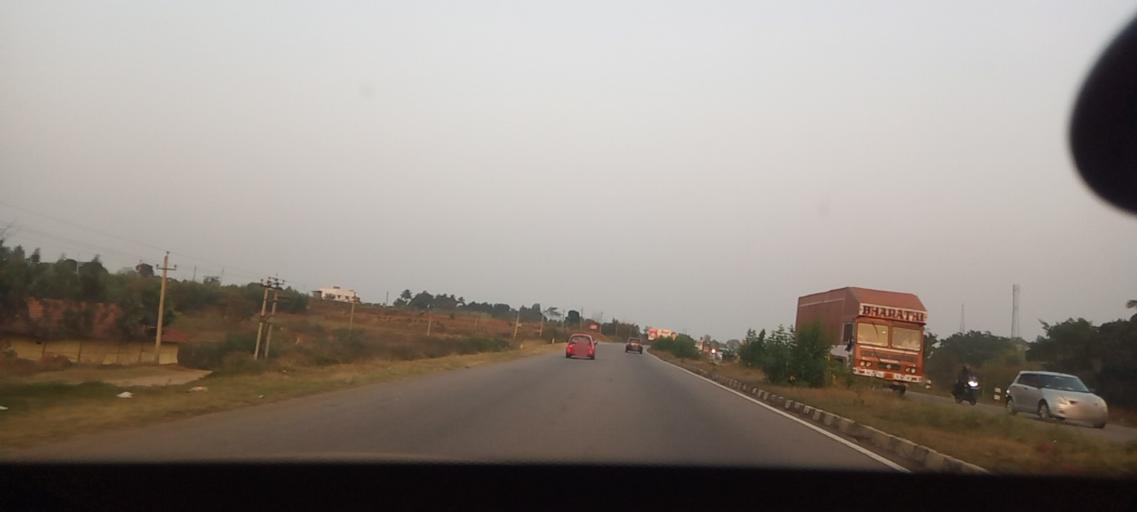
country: IN
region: Karnataka
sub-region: Ramanagara
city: Magadi
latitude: 13.0774
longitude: 77.2030
